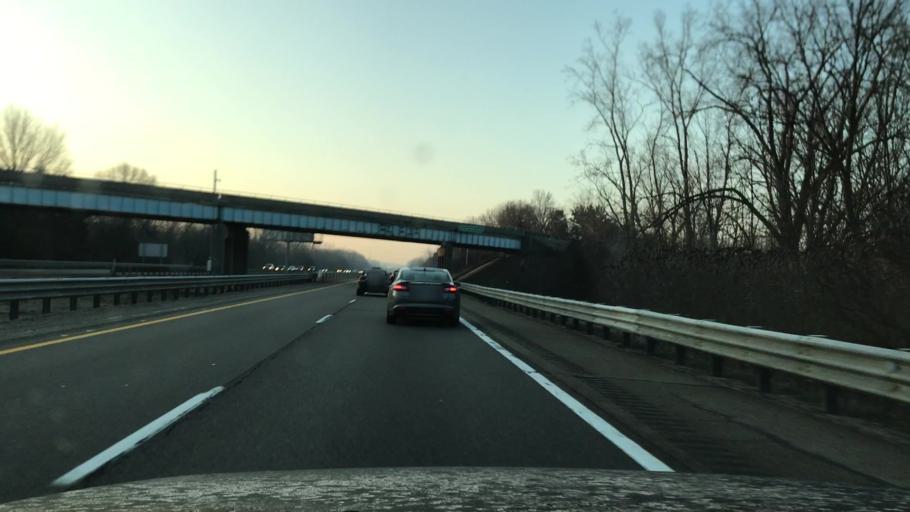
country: US
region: Michigan
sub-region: Kent County
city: East Grand Rapids
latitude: 42.9294
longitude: -85.5608
